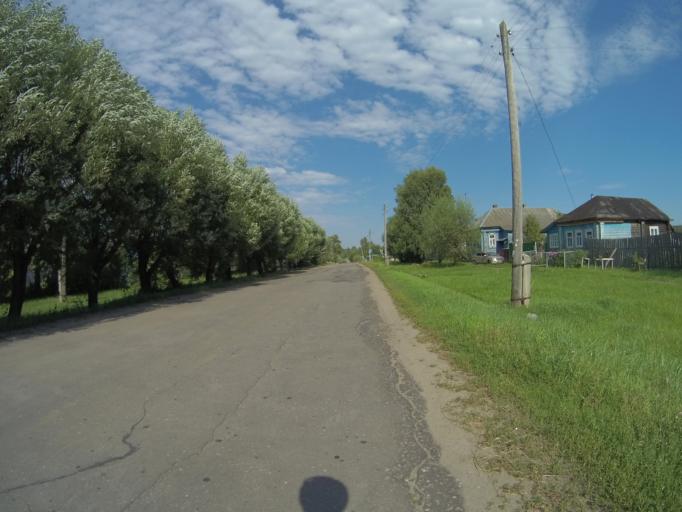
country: RU
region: Vladimir
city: Orgtrud
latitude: 56.0339
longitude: 40.6792
